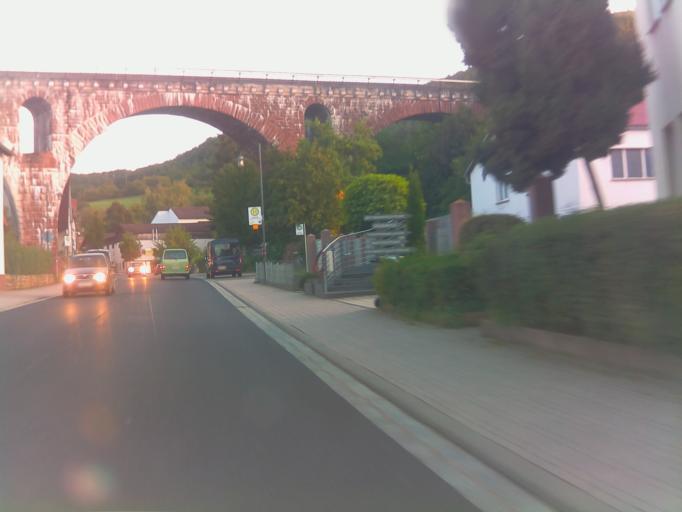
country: DE
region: Bavaria
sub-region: Regierungsbezirk Unterfranken
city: Euerdorf
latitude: 50.1470
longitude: 10.0237
